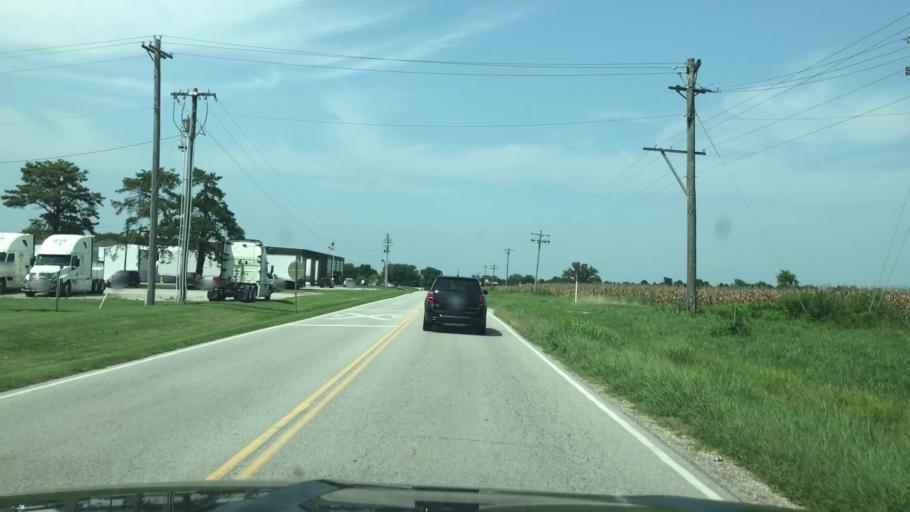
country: US
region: Oklahoma
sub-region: Ottawa County
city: Commerce
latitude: 36.9143
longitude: -94.8419
